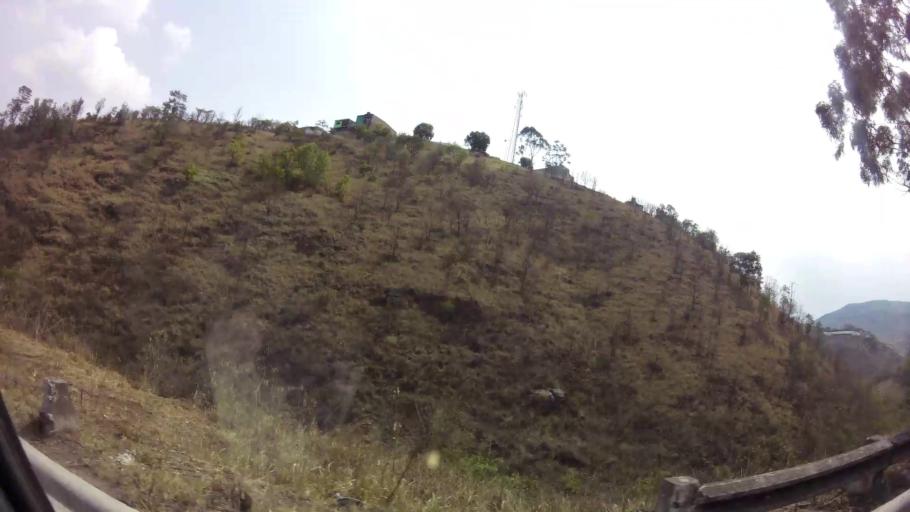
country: HN
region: Francisco Morazan
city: Tegucigalpa
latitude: 14.1194
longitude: -87.2197
